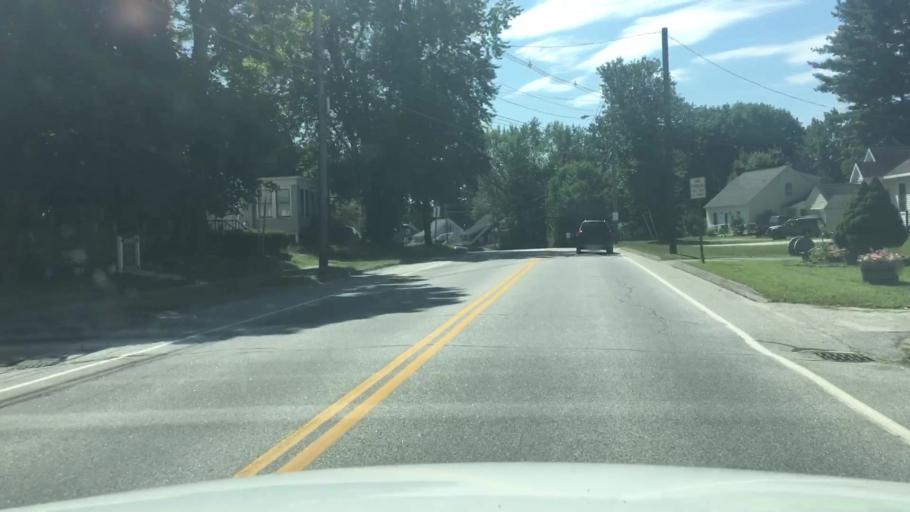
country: US
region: Maine
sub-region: Androscoggin County
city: Auburn
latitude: 44.1109
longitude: -70.2332
